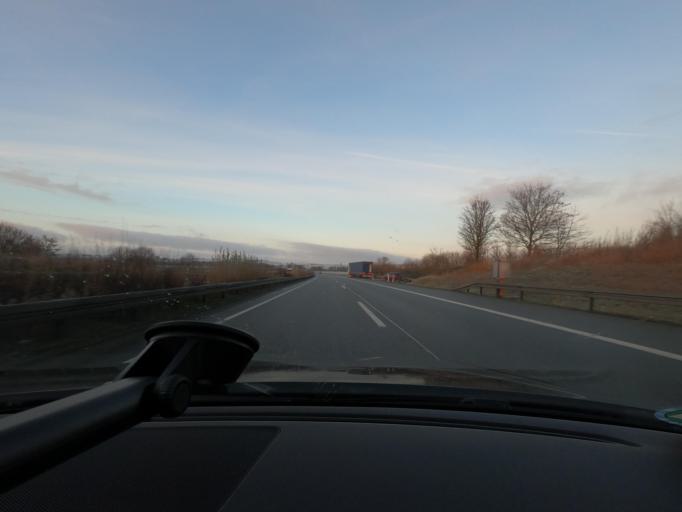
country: DE
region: Thuringia
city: Breitenworbis
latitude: 51.4036
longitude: 10.4127
